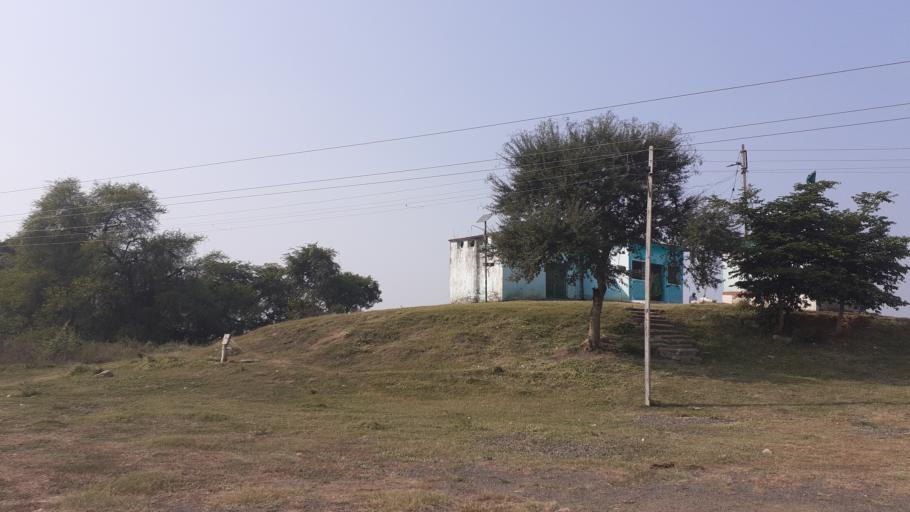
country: IN
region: Maharashtra
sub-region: Chandrapur
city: Warora
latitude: 20.3188
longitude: 79.1159
